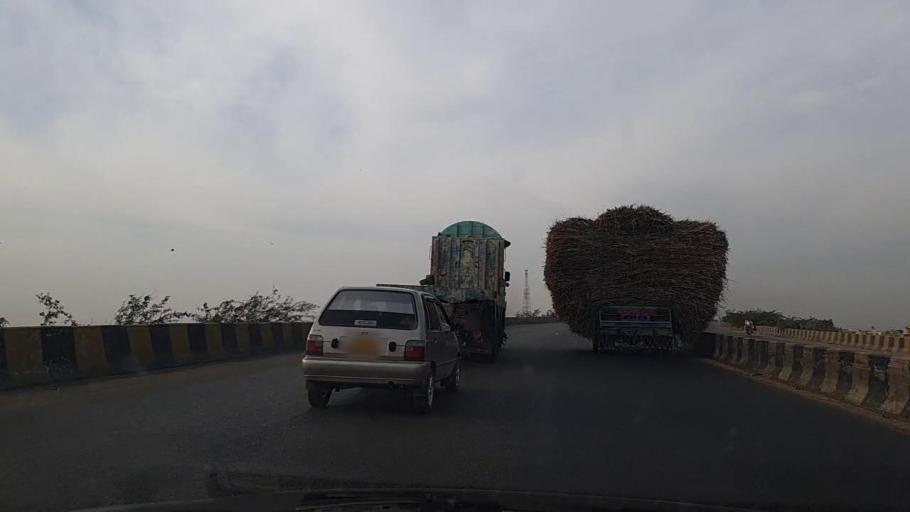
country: PK
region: Sindh
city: Gharo
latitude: 24.8425
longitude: 67.4309
